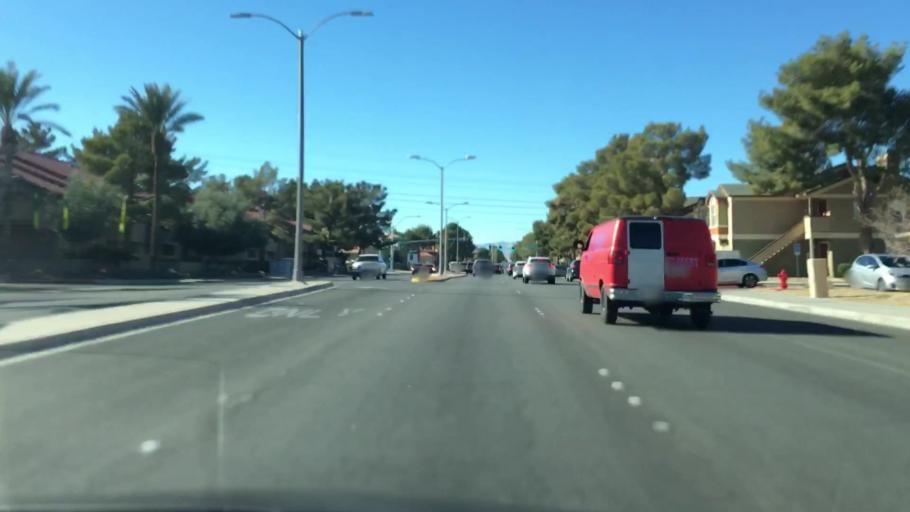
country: US
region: Nevada
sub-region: Clark County
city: Whitney
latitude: 36.0565
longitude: -115.0820
